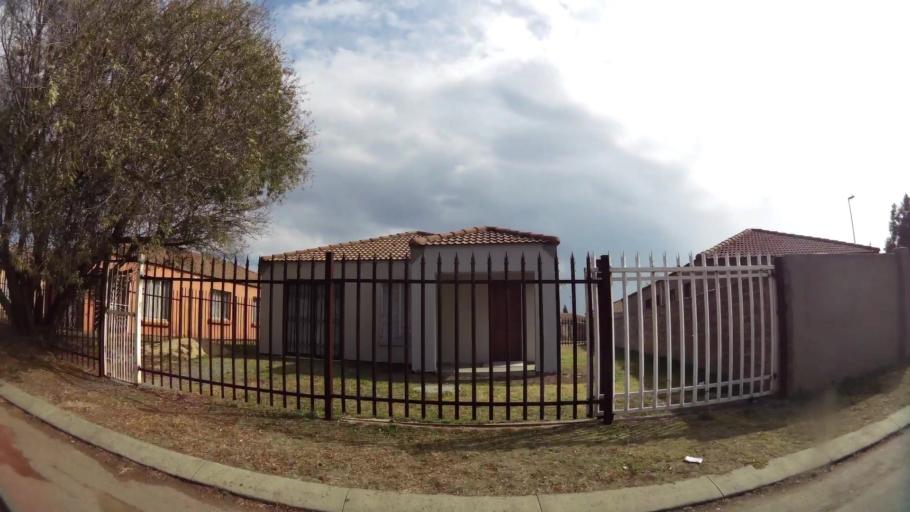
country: ZA
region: Gauteng
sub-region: Sedibeng District Municipality
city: Vanderbijlpark
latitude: -26.7163
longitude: 27.8859
